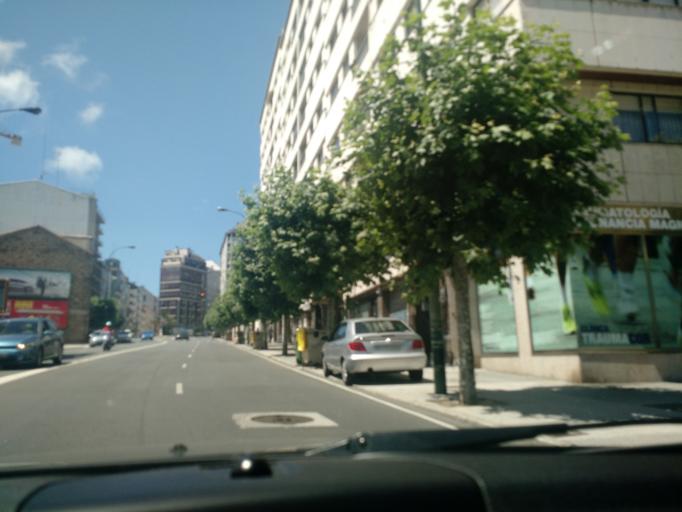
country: ES
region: Galicia
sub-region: Provincia da Coruna
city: A Coruna
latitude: 43.3595
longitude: -8.4126
